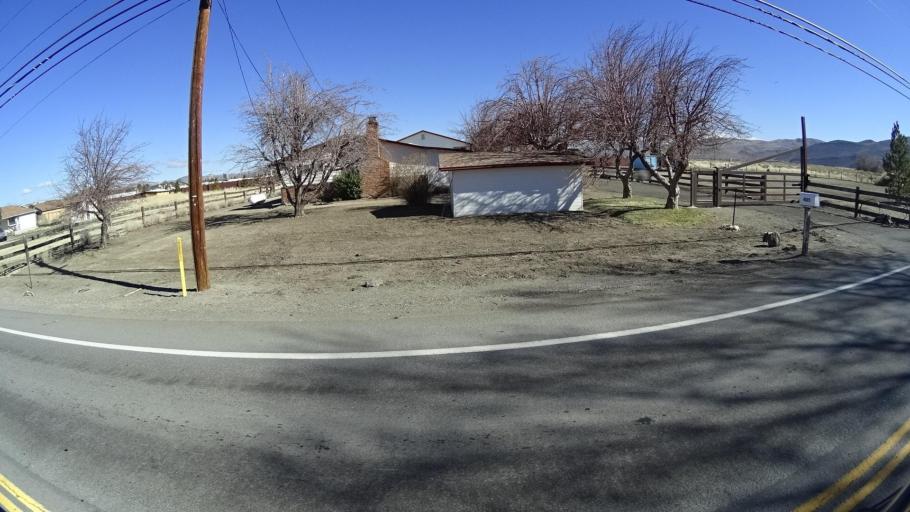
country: US
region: Nevada
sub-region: Washoe County
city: Sparks
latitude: 39.4974
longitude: -119.7462
